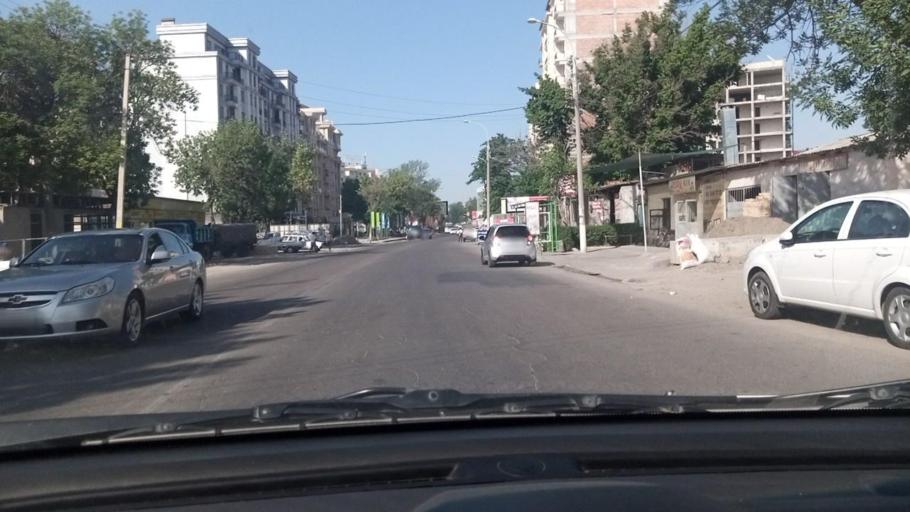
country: UZ
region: Toshkent
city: Salor
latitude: 41.3144
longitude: 69.3344
